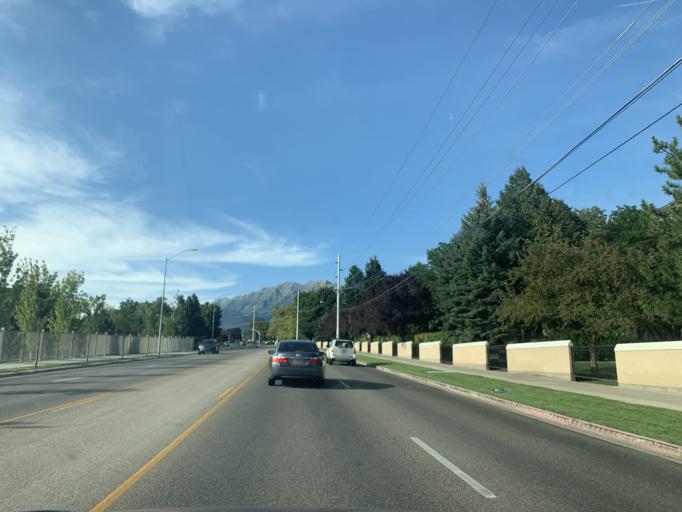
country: US
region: Utah
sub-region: Utah County
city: Provo
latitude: 40.2580
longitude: -111.6432
